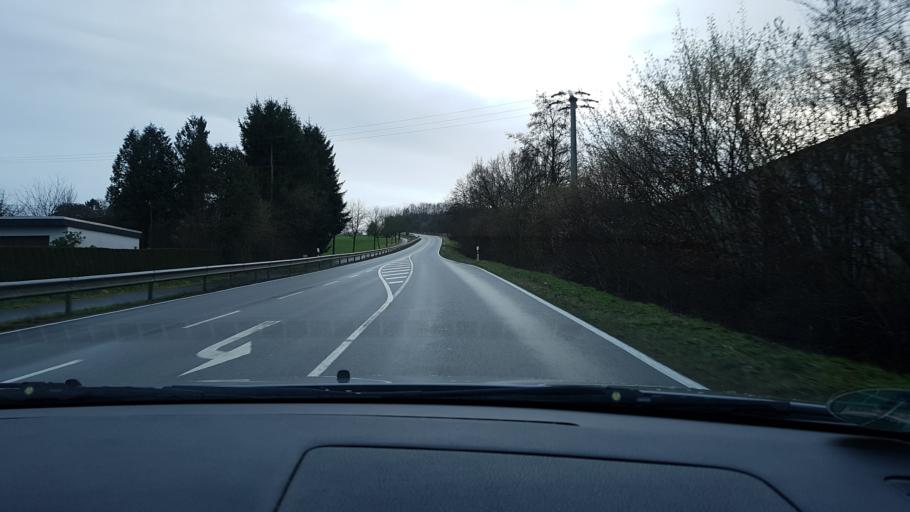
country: DE
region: Rheinland-Pfalz
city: Niederelbert
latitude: 50.4006
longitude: 7.8119
